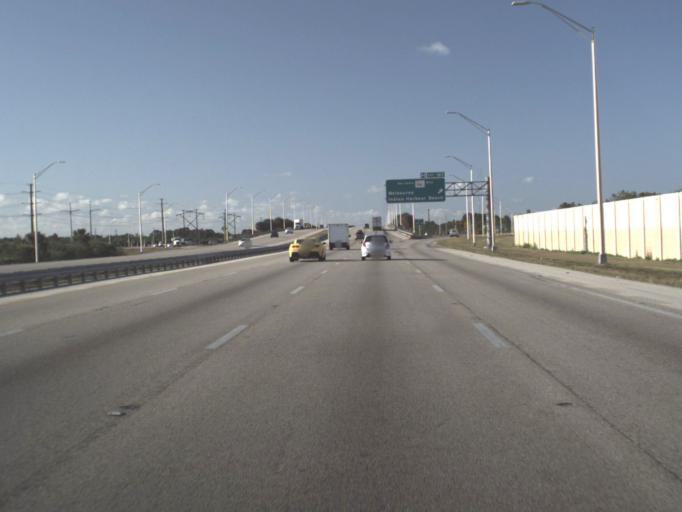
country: US
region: Florida
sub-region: Brevard County
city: June Park
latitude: 28.1158
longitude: -80.7058
